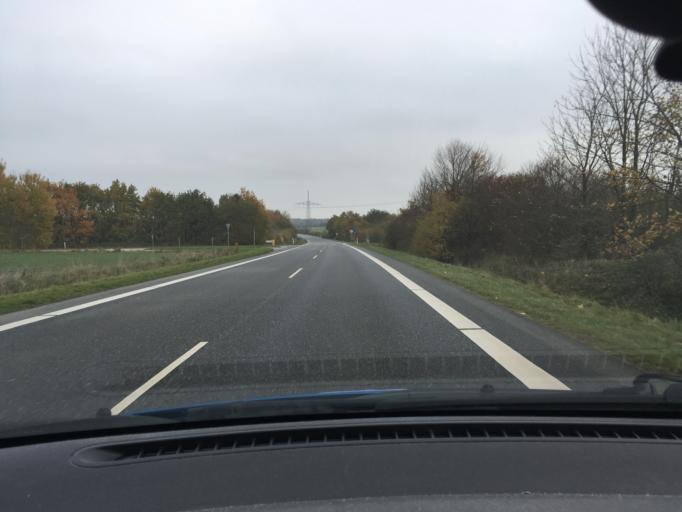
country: DK
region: South Denmark
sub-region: Aabenraa Kommune
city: Aabenraa
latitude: 54.9898
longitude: 9.4053
